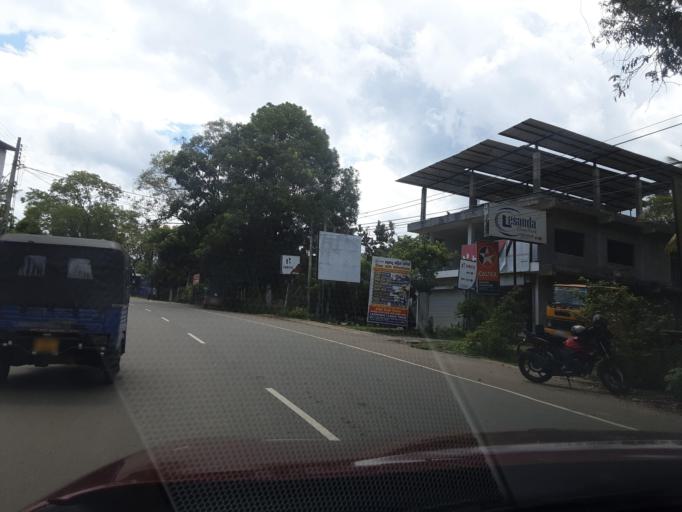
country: LK
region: Uva
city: Monaragala
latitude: 6.8978
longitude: 81.2395
